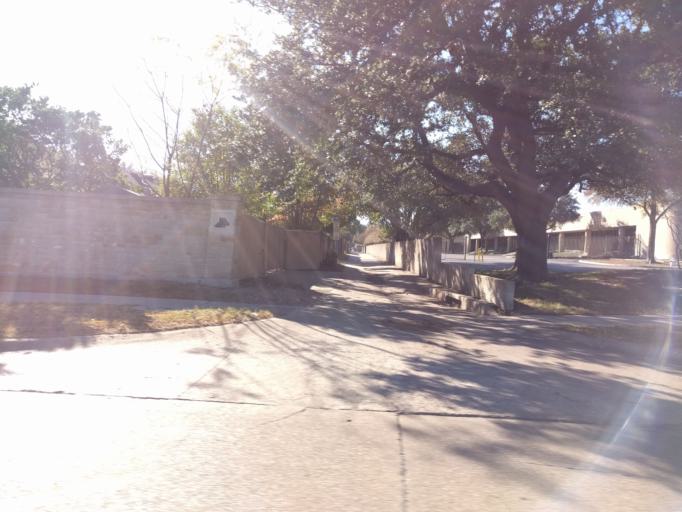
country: US
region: Texas
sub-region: Dallas County
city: Richardson
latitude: 32.9781
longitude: -96.7605
